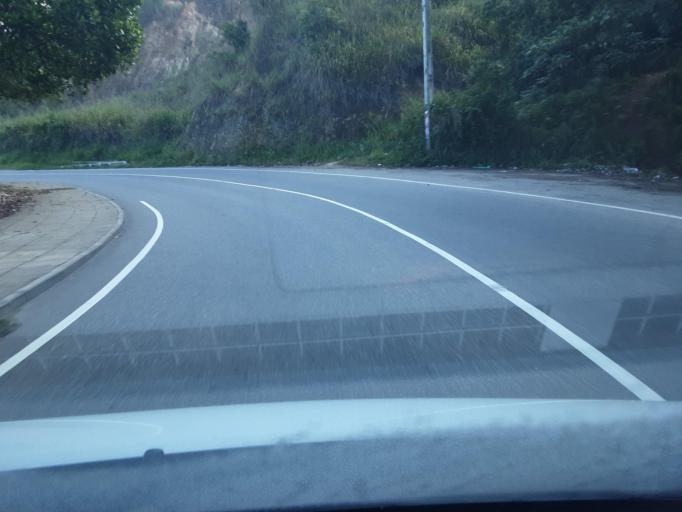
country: LK
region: Uva
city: Haputale
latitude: 6.9076
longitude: 80.9203
